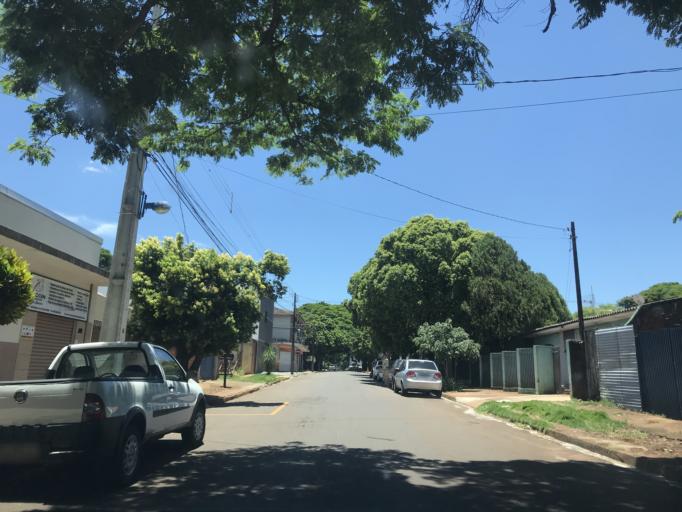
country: BR
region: Parana
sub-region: Sarandi
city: Sarandi
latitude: -23.4397
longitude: -51.8949
